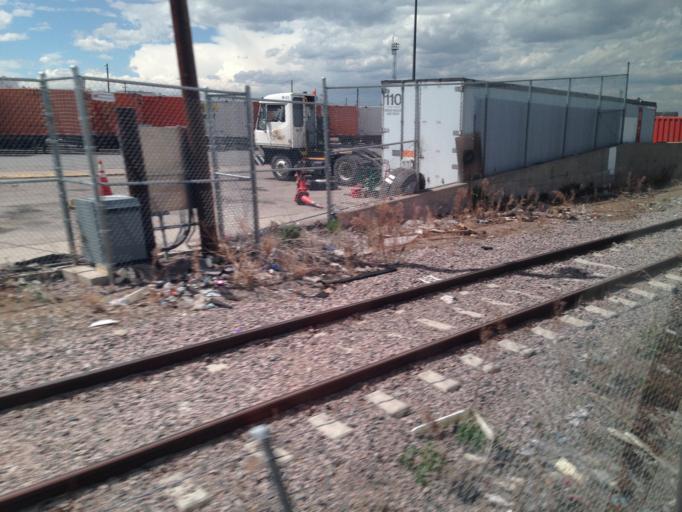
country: US
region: Colorado
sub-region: Adams County
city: Berkley
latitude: 39.7844
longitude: -104.9967
